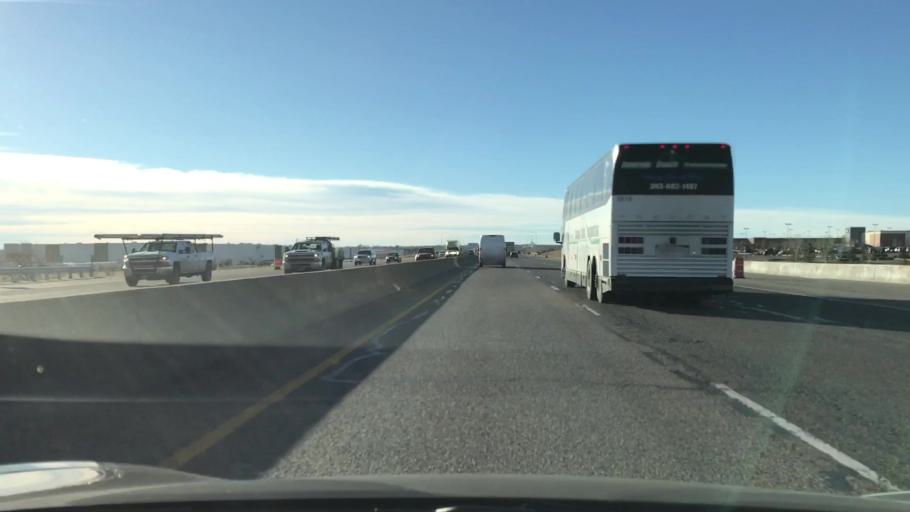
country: US
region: Colorado
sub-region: Adams County
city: Northglenn
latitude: 39.9681
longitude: -104.9882
